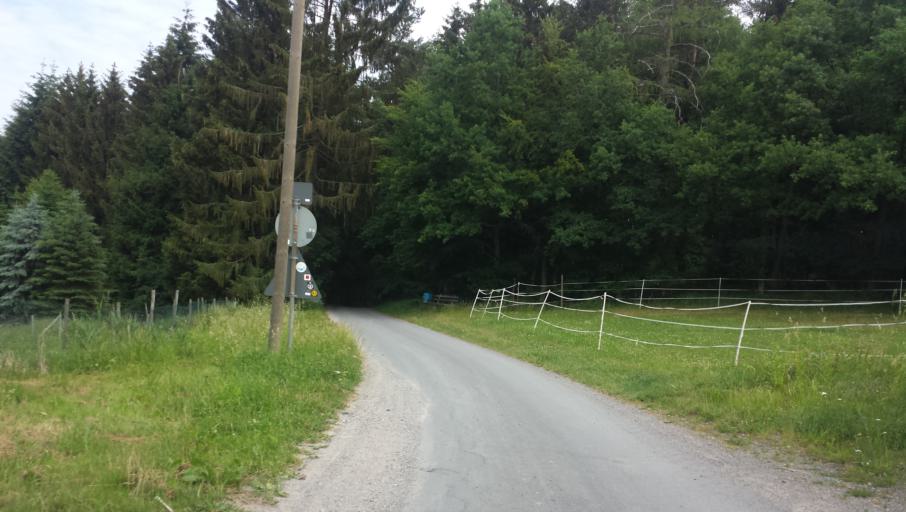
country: DE
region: Hesse
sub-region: Regierungsbezirk Darmstadt
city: Furth
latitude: 49.6246
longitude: 8.8112
